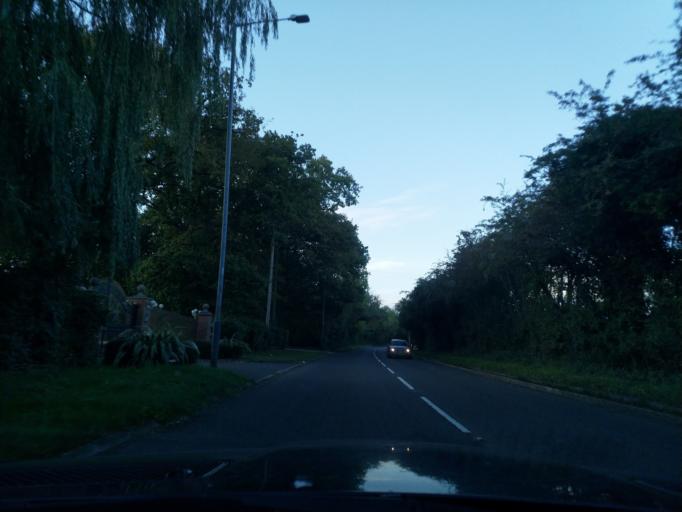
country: GB
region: England
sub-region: Warwickshire
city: Henley in Arden
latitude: 52.3393
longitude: -1.7738
